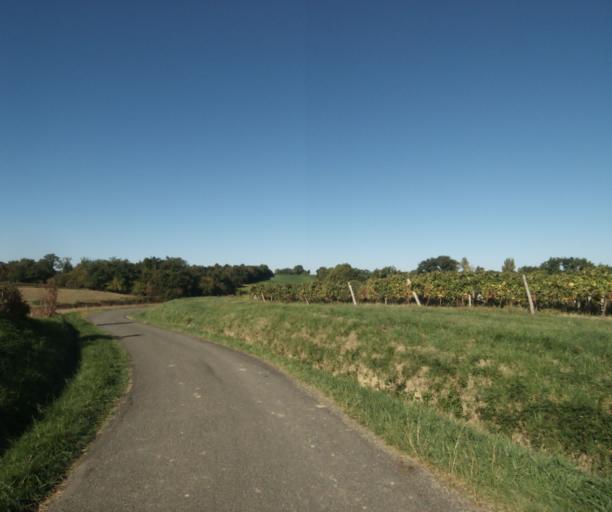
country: FR
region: Midi-Pyrenees
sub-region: Departement du Gers
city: Gondrin
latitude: 43.8132
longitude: 0.2016
